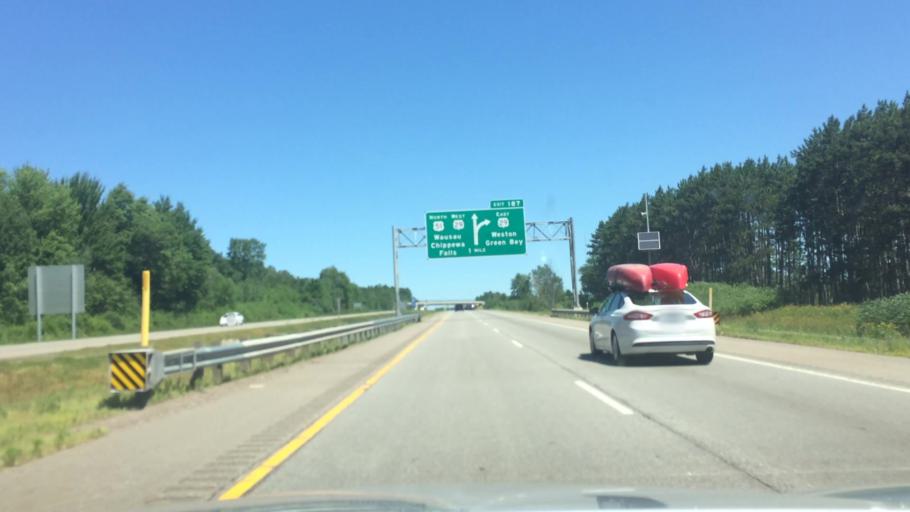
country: US
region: Wisconsin
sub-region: Marathon County
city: Rothschild
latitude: 44.8740
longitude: -89.6447
